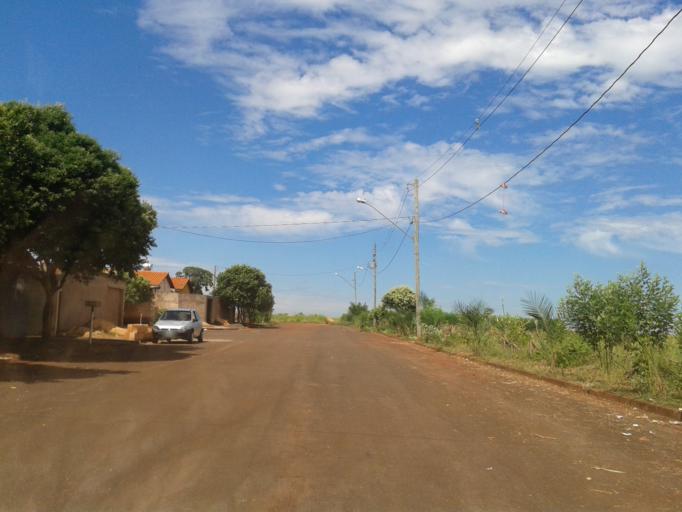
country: BR
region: Minas Gerais
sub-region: Capinopolis
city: Capinopolis
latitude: -18.5221
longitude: -49.5039
